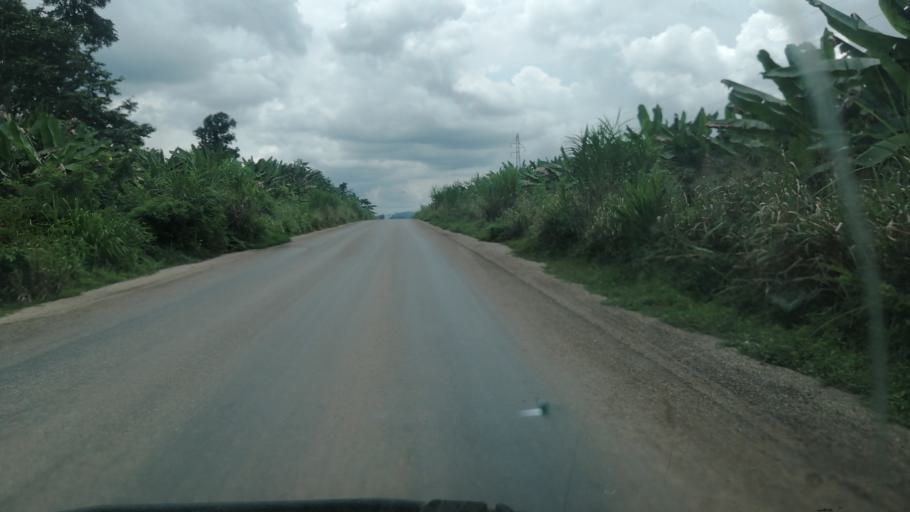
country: GH
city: Duayaw Nkwanta
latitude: 6.9082
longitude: -2.3952
